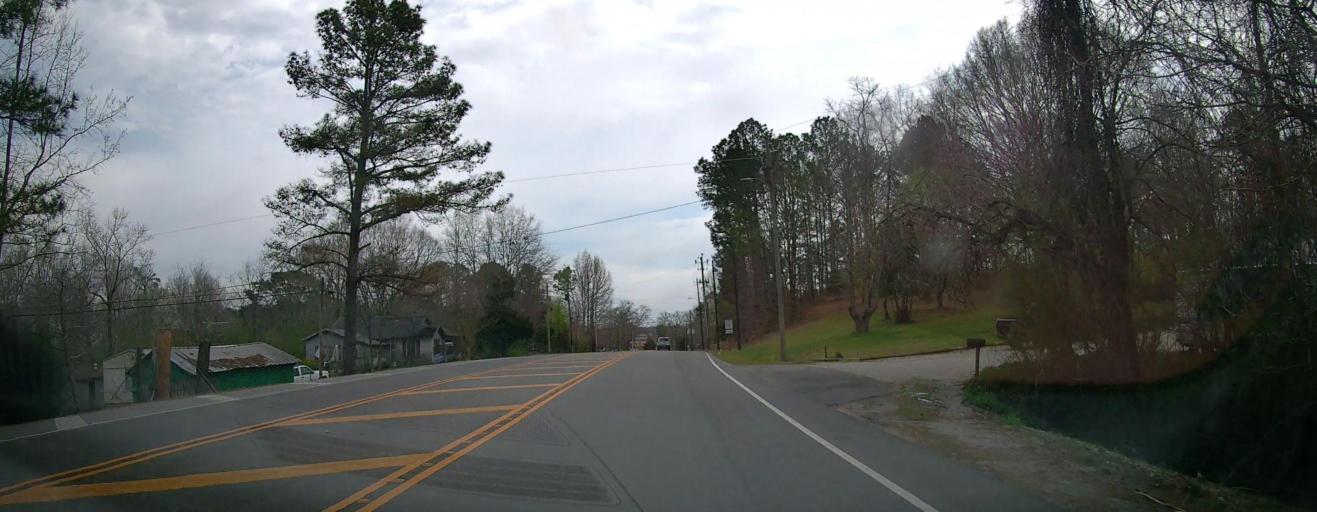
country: US
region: Alabama
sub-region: Marion County
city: Guin
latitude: 33.9820
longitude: -87.9178
